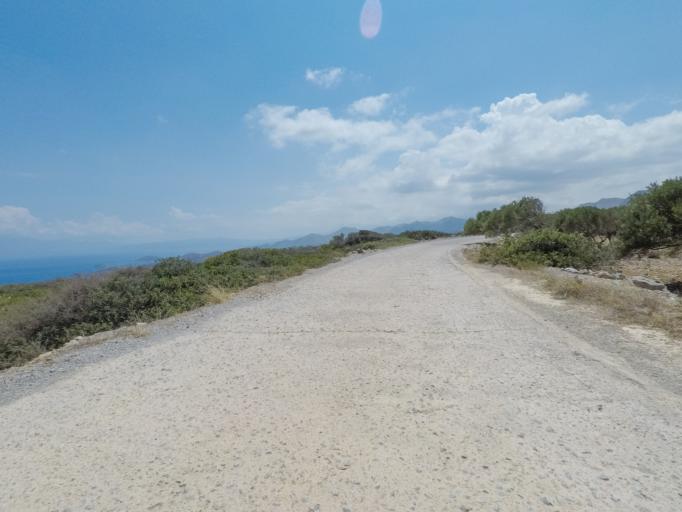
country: GR
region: Crete
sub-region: Nomos Lasithiou
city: Elounda
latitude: 35.3170
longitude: 25.7481
